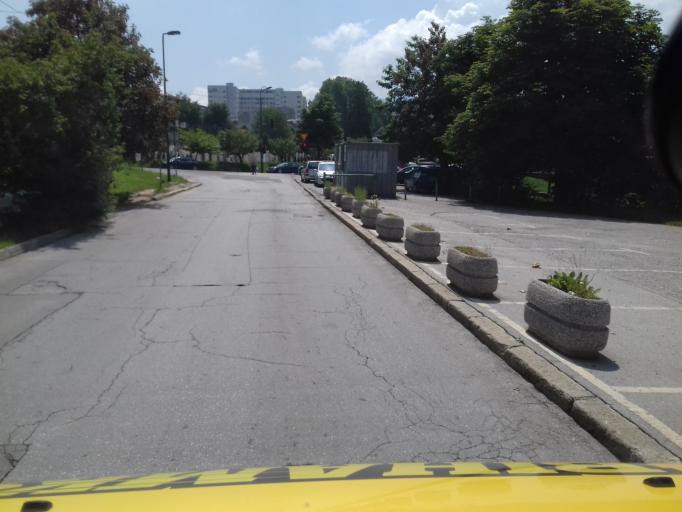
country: BA
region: Federation of Bosnia and Herzegovina
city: Kobilja Glava
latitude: 43.8726
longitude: 18.4114
